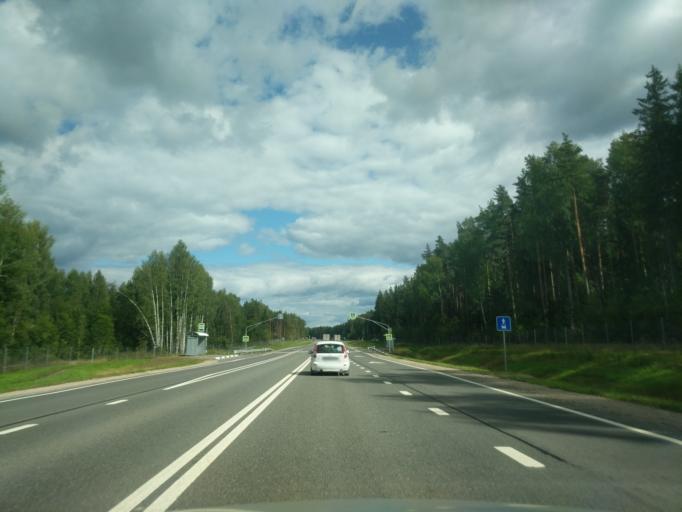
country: RU
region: Kostroma
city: Oktyabr'skiy
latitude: 57.7983
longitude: 41.2465
